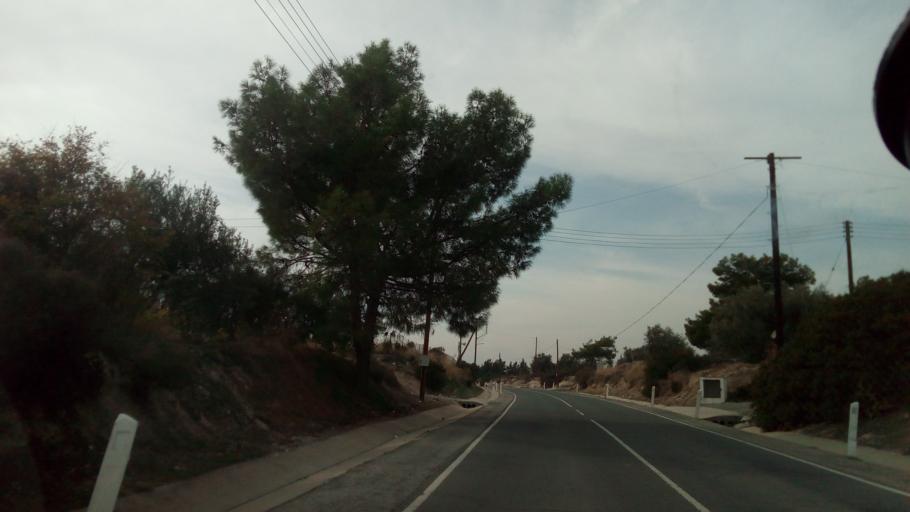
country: CY
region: Larnaka
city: Tersefanou
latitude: 34.8636
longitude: 33.4829
